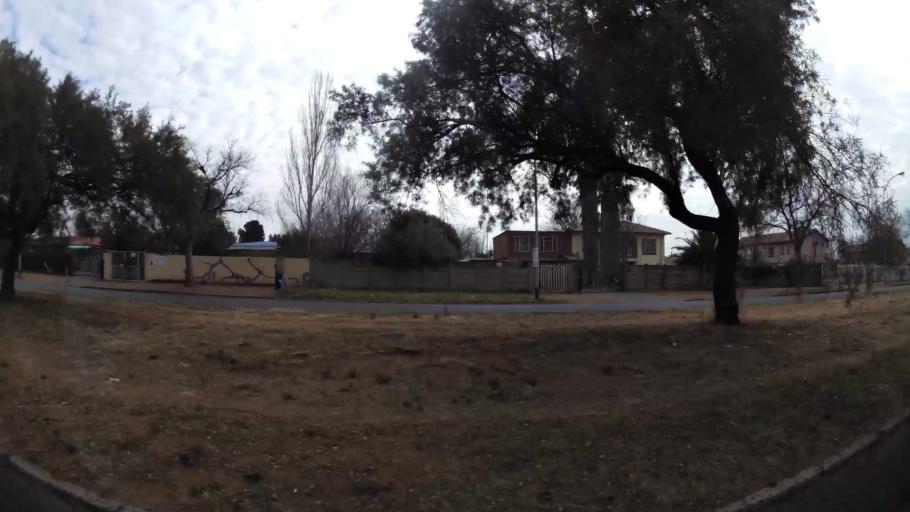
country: ZA
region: Orange Free State
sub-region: Mangaung Metropolitan Municipality
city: Bloemfontein
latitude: -29.1312
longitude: 26.1881
